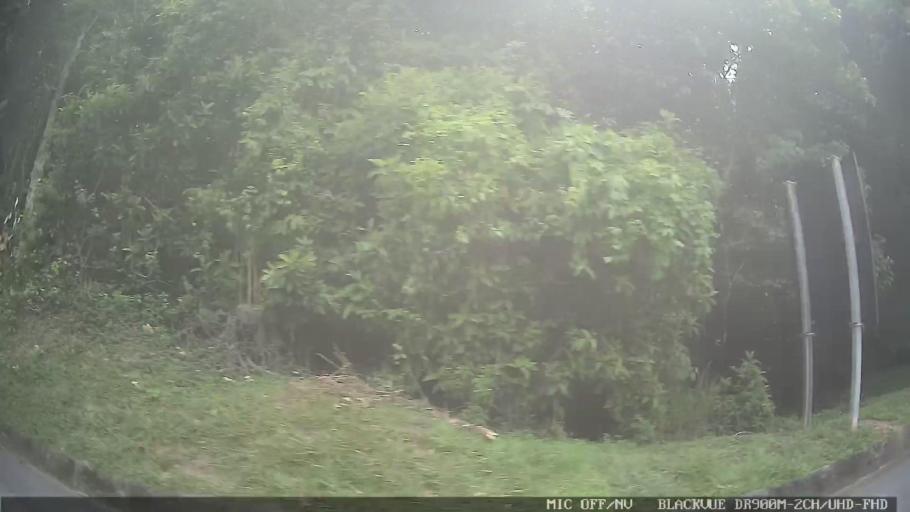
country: BR
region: Sao Paulo
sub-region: Caraguatatuba
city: Caraguatatuba
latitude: -23.5995
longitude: -45.4305
